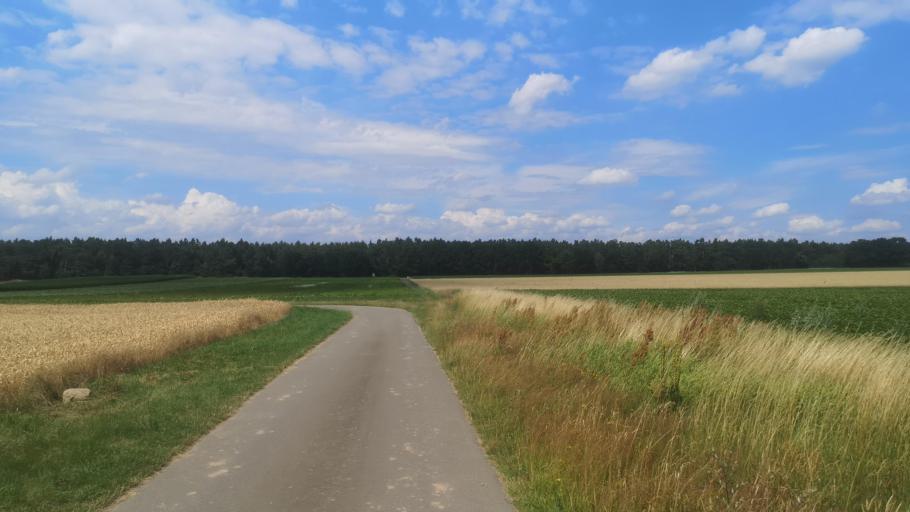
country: DE
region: Lower Saxony
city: Dahlem
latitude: 53.2315
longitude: 10.7461
